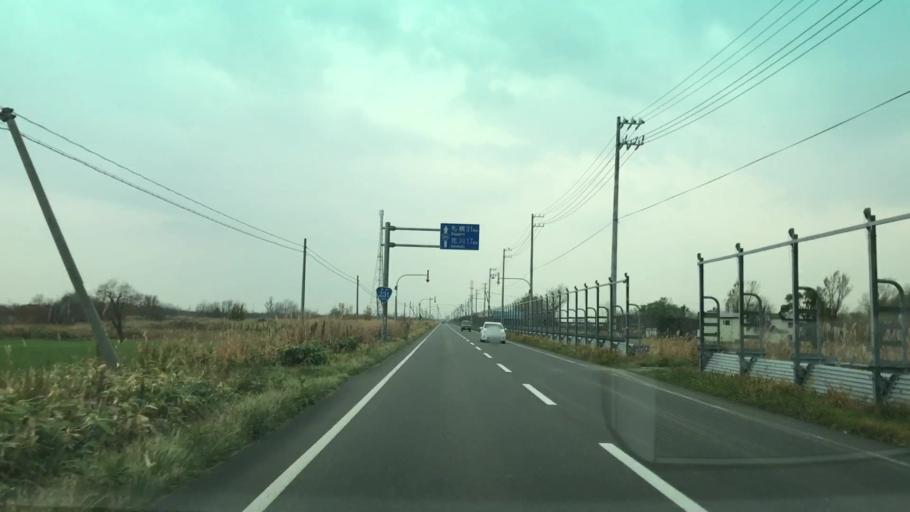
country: JP
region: Hokkaido
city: Ishikari
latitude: 43.2954
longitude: 141.4111
